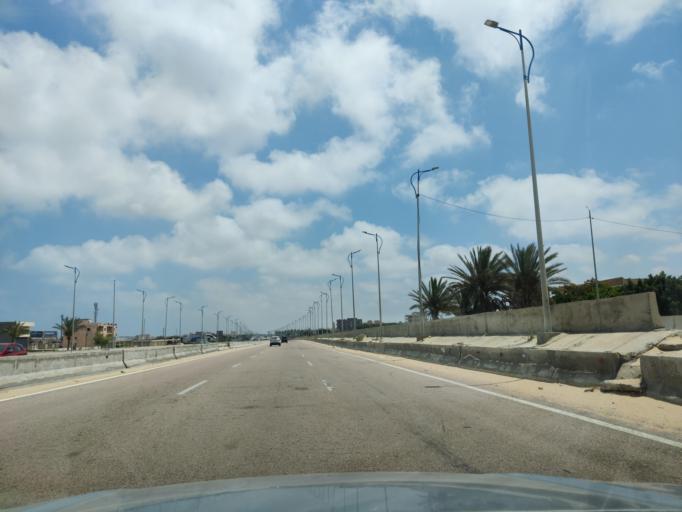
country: EG
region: Alexandria
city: Alexandria
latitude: 30.9737
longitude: 29.5680
